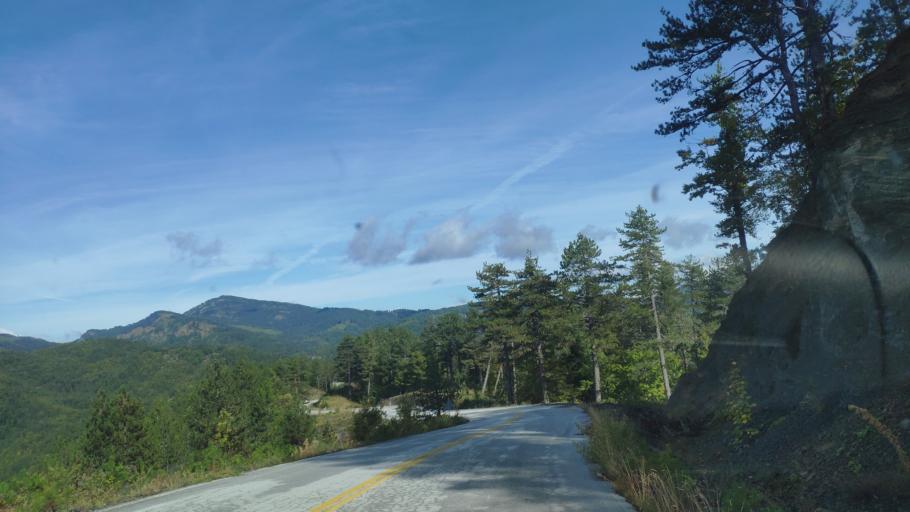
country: GR
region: West Macedonia
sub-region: Nomos Kastorias
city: Nestorio
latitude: 40.3644
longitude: 20.9473
